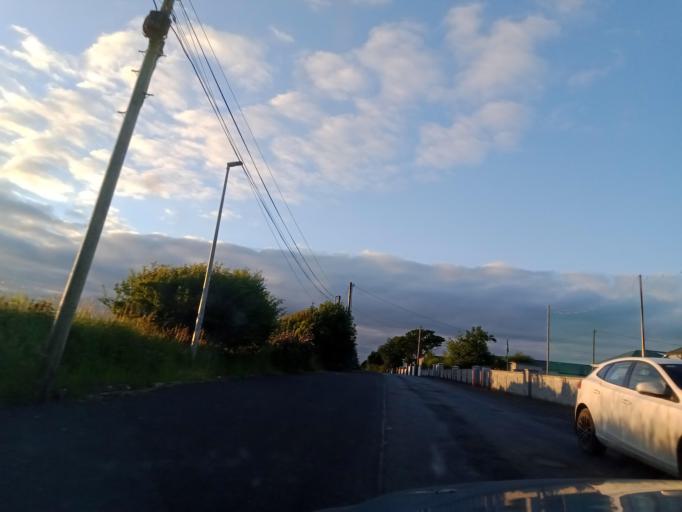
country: IE
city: Ballylinan
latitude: 52.8999
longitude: -7.1320
